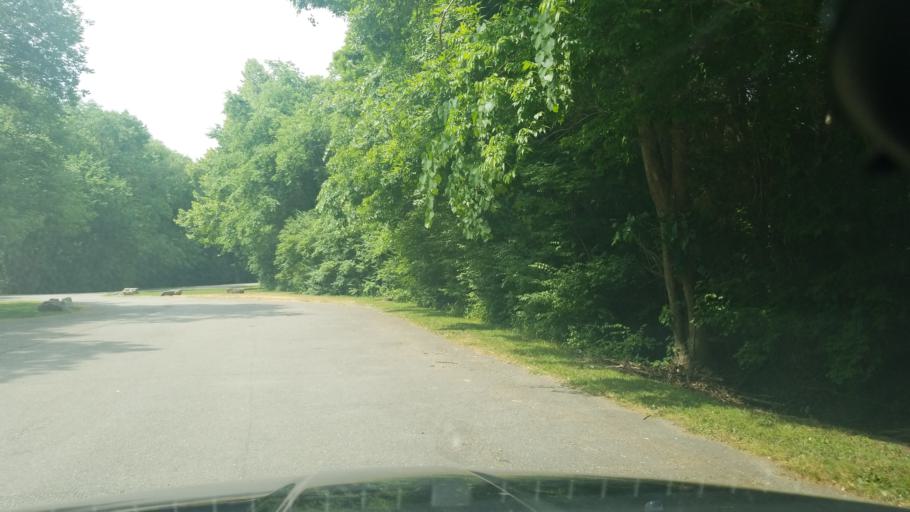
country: US
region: Tennessee
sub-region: Davidson County
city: Goodlettsville
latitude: 36.2723
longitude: -86.7483
